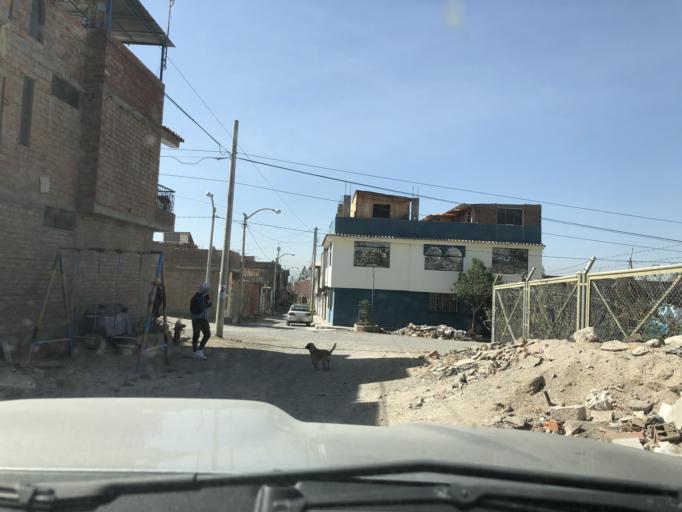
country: PE
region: Arequipa
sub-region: Provincia de Arequipa
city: Arequipa
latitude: -16.3430
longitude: -71.5525
